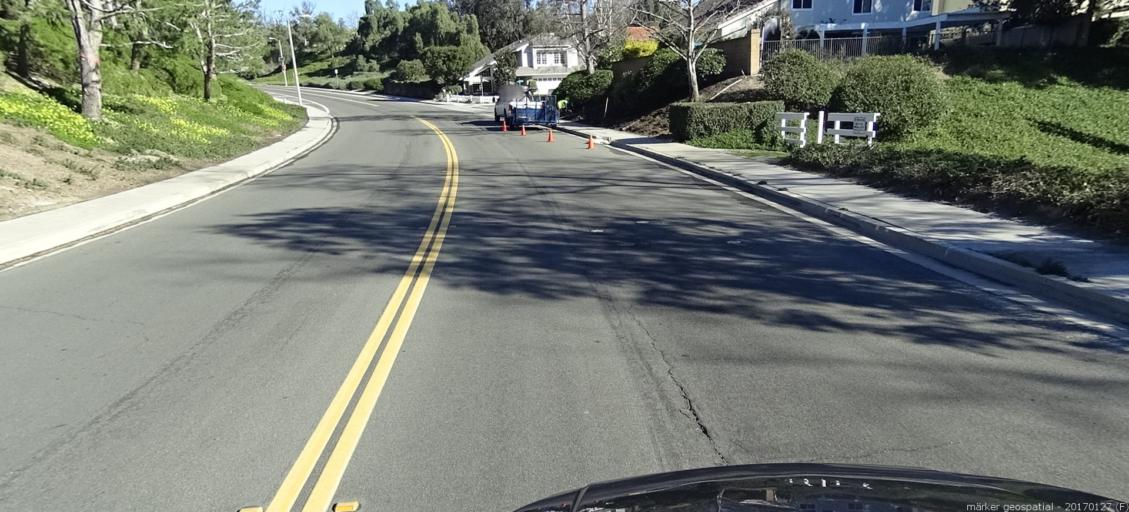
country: US
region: California
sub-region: Orange County
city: Foothill Ranch
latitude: 33.6586
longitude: -117.6600
